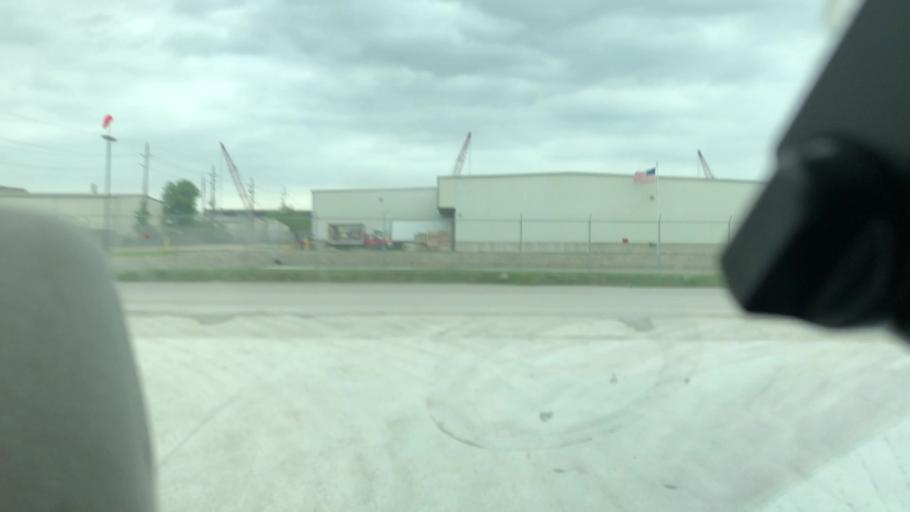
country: US
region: Texas
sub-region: Harris County
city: Jersey Village
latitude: 29.8755
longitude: -95.5800
